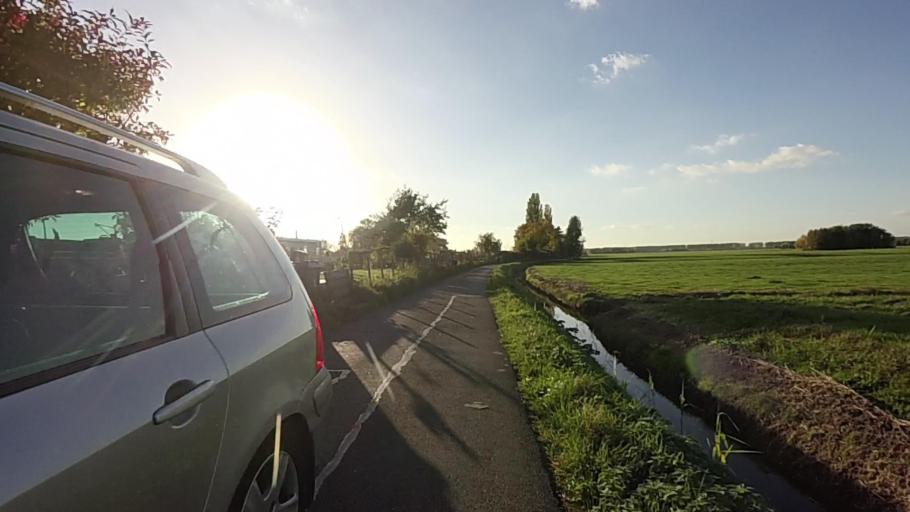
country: NL
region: Utrecht
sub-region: Stichtse Vecht
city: Vreeland
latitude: 52.2475
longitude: 5.0432
